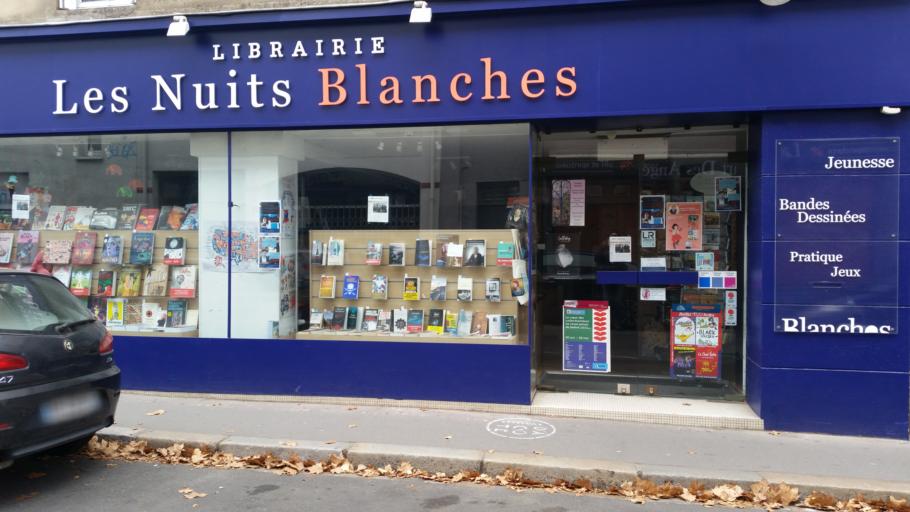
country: FR
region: Pays de la Loire
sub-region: Departement de la Loire-Atlantique
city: Nantes
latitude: 47.2221
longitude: -1.5627
